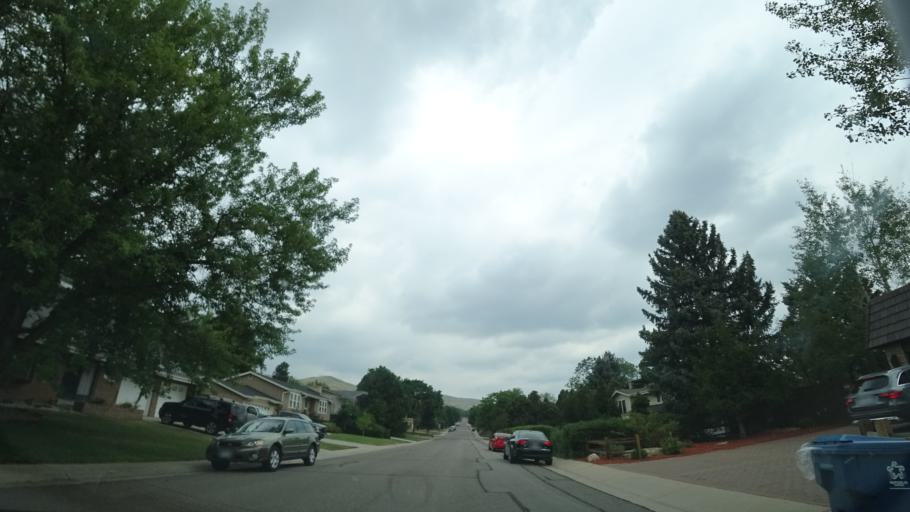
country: US
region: Colorado
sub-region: Jefferson County
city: West Pleasant View
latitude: 39.7094
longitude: -105.1483
